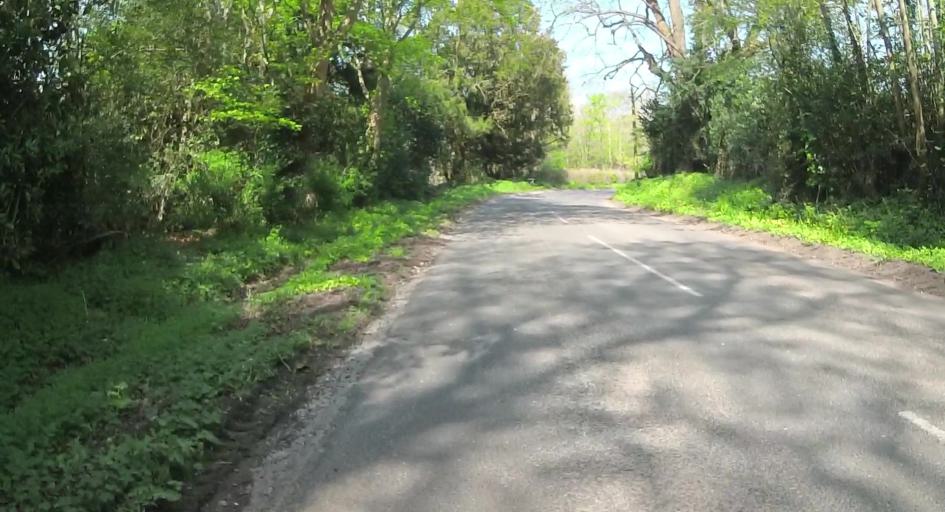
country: GB
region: England
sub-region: Hampshire
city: Basingstoke
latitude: 51.3043
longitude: -1.0883
